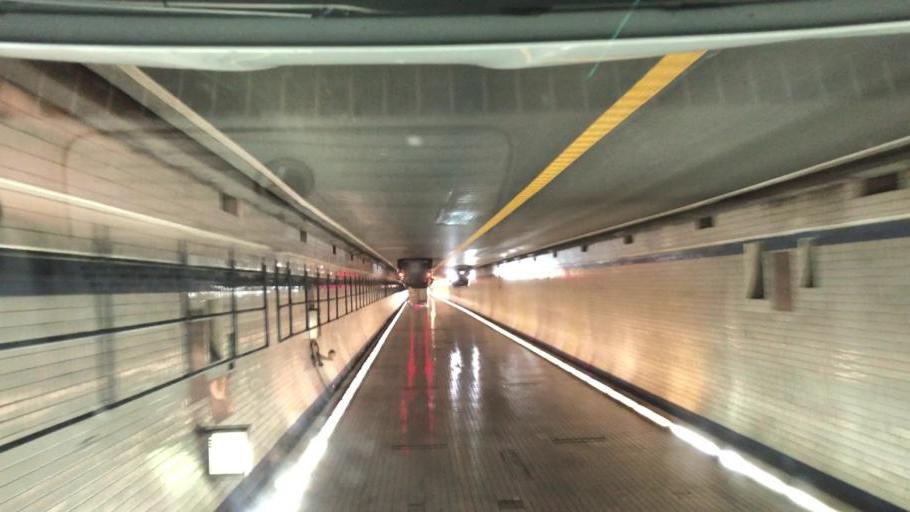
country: US
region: Virginia
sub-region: City of Virginia Beach
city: Virginia Beach
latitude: 37.0376
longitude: -76.0757
